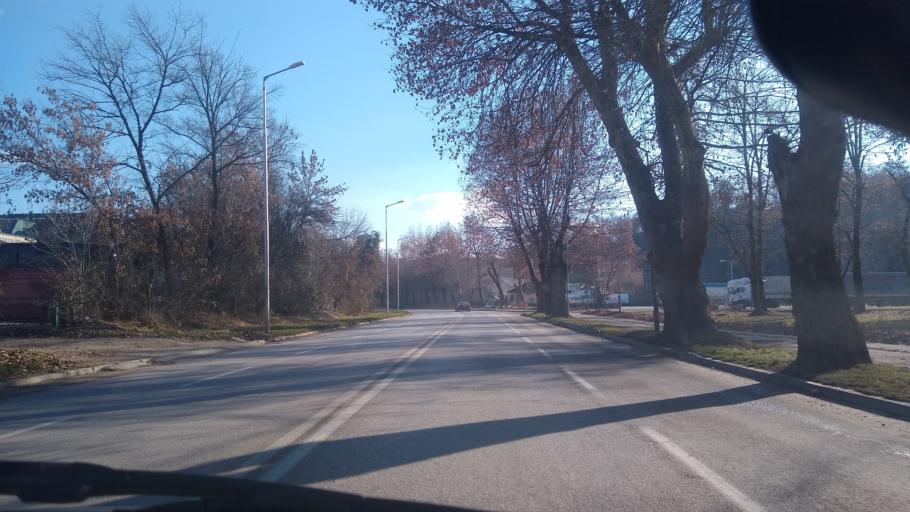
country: MK
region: Bitola
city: Bitola
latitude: 41.0177
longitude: 21.3422
